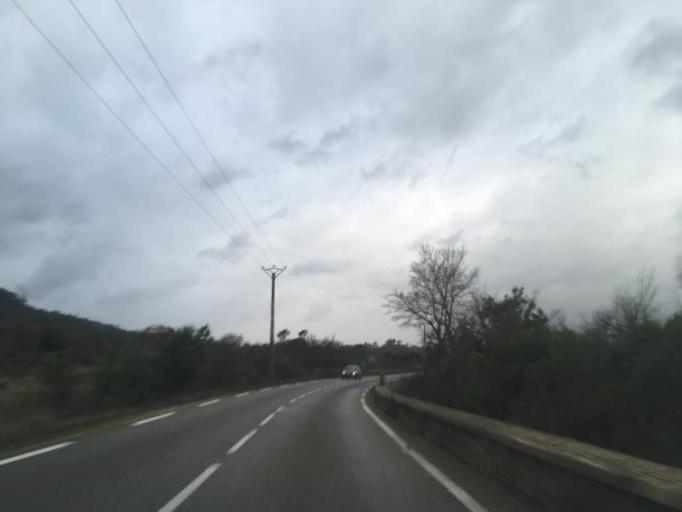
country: FR
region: Provence-Alpes-Cote d'Azur
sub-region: Departement du Var
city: Sainte-Anastasie-sur-Issole
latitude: 43.3387
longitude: 6.1122
